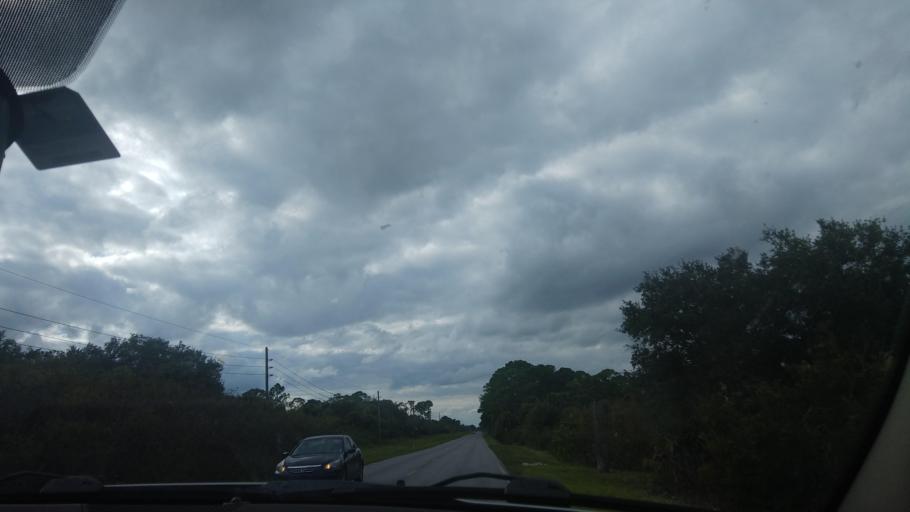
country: US
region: Florida
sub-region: Saint Lucie County
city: Lakewood Park
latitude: 27.5207
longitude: -80.3614
